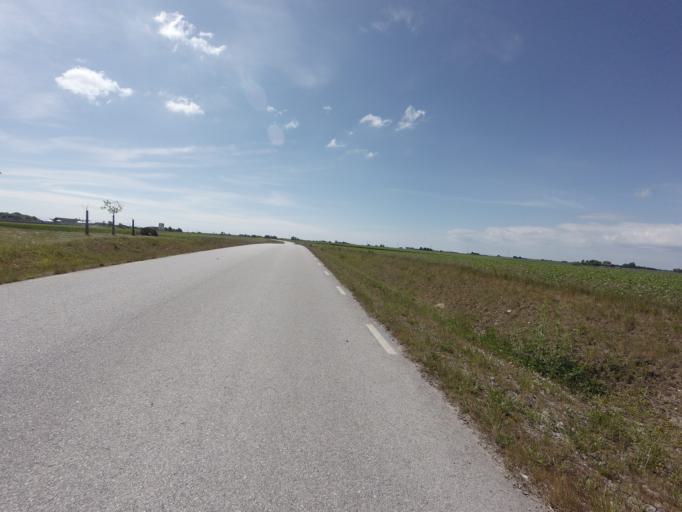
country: SE
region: Skane
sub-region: Trelleborgs Kommun
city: Skare
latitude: 55.4109
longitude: 13.0601
